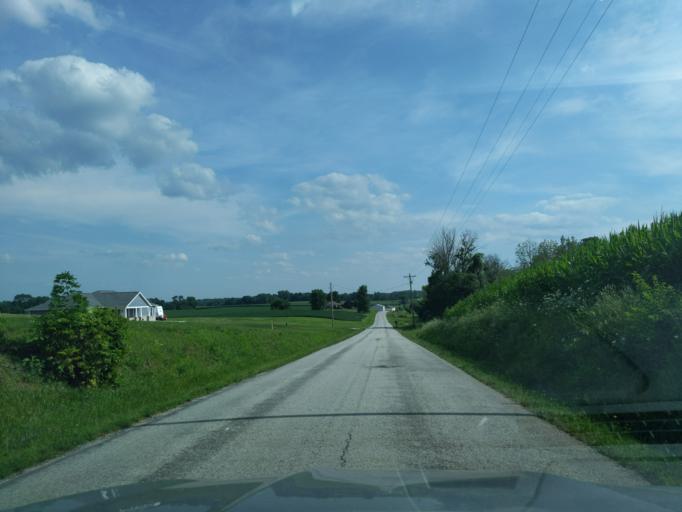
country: US
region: Indiana
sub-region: Decatur County
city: Greensburg
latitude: 39.2670
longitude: -85.4651
